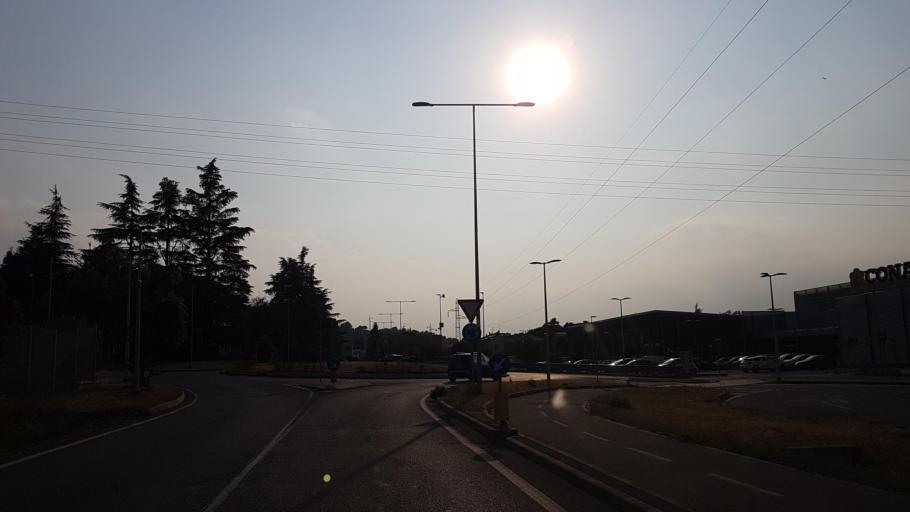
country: IT
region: Emilia-Romagna
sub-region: Provincia di Parma
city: Ricco
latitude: 44.7030
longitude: 10.1272
